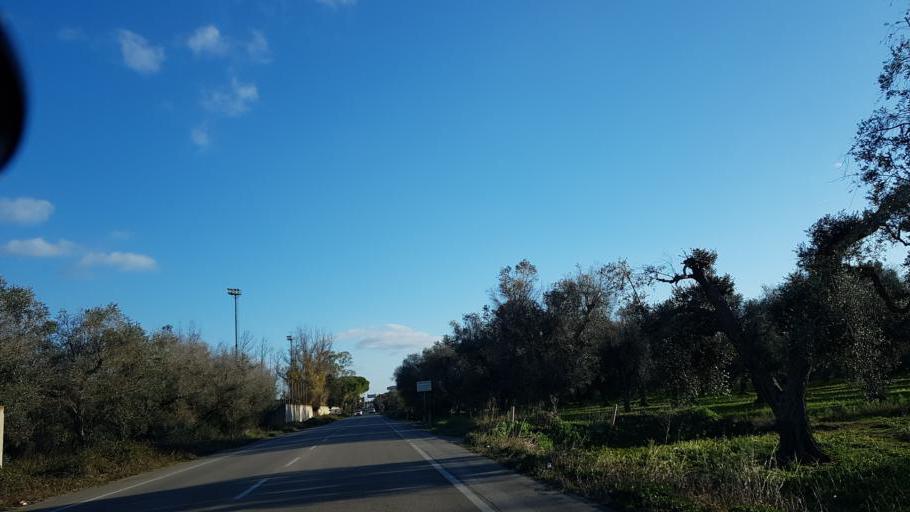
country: IT
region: Apulia
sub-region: Provincia di Lecce
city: Squinzano
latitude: 40.4458
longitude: 18.0322
